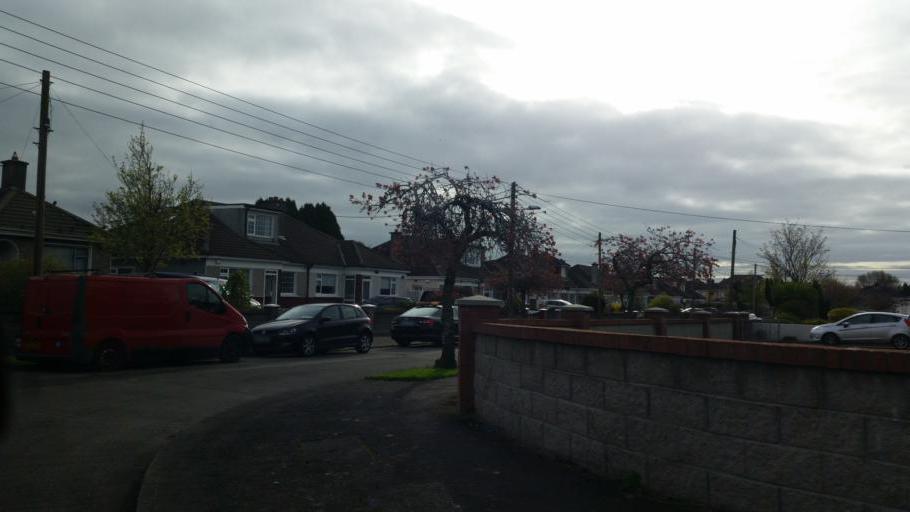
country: IE
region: Leinster
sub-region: Dublin City
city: Finglas
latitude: 53.3957
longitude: -6.2868
